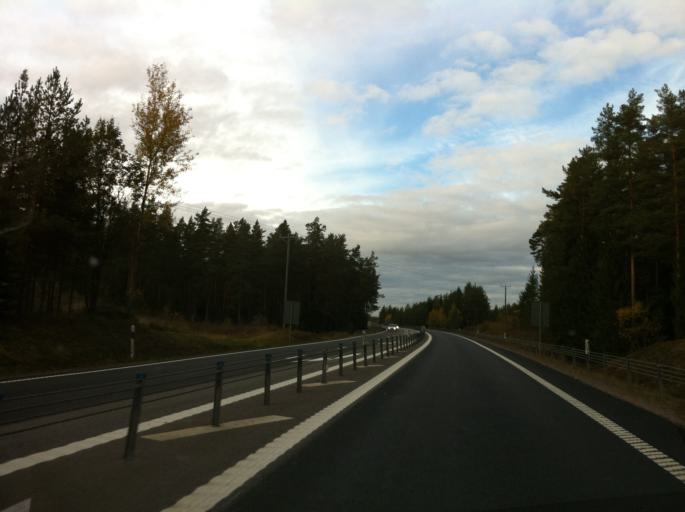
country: SE
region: OErebro
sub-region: Askersunds Kommun
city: Asbro
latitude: 58.9807
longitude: 15.0391
